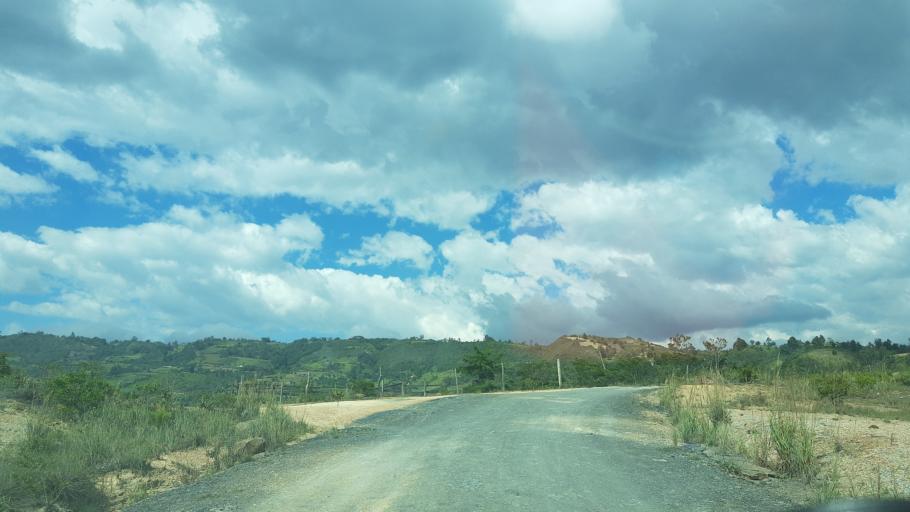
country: CO
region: Boyaca
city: Santa Sofia
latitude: 5.7066
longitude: -73.5437
